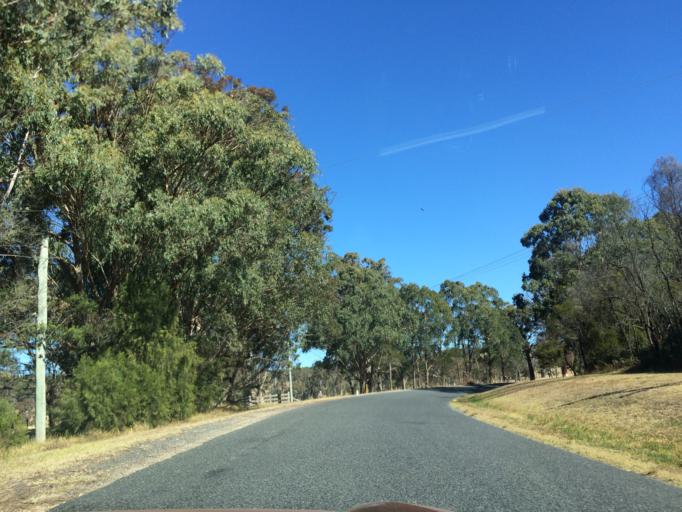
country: AU
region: Queensland
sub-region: Southern Downs
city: Stanthorpe
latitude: -28.6506
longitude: 152.0842
